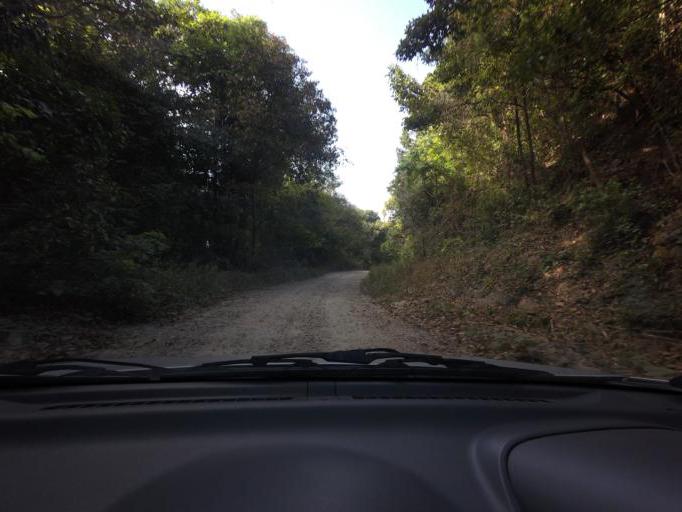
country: IN
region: Karnataka
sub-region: Kodagu
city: Somvarpet
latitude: 12.7116
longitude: 75.6881
